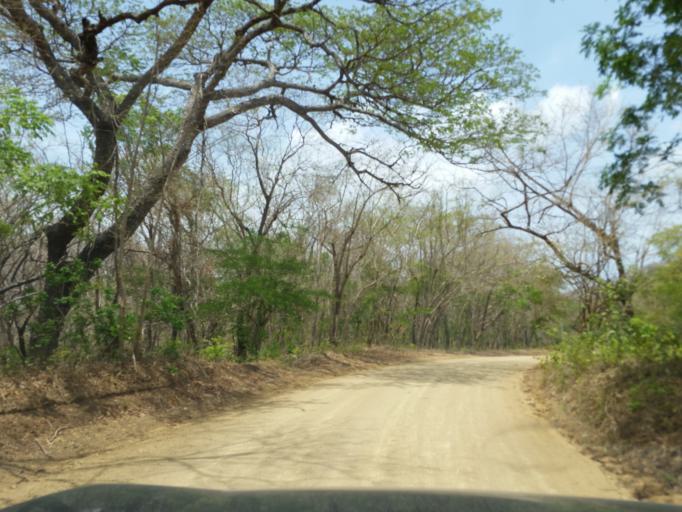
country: NI
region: Rivas
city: Tola
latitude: 11.4369
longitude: -86.0776
